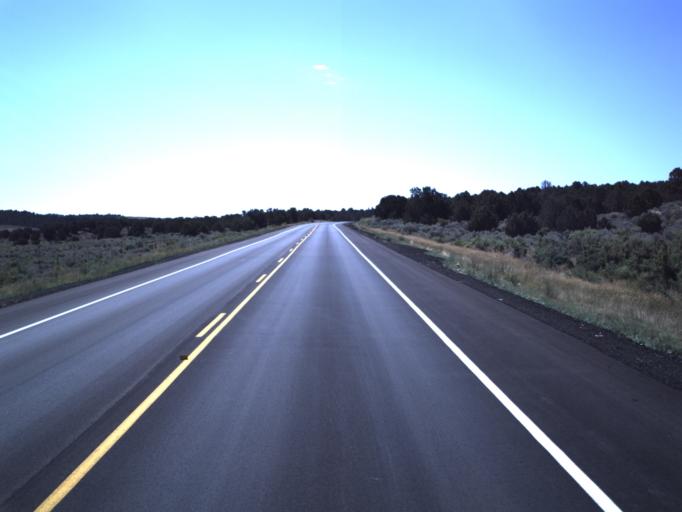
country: US
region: Utah
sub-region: Utah County
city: Eagle Mountain
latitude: 40.0138
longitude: -112.2776
